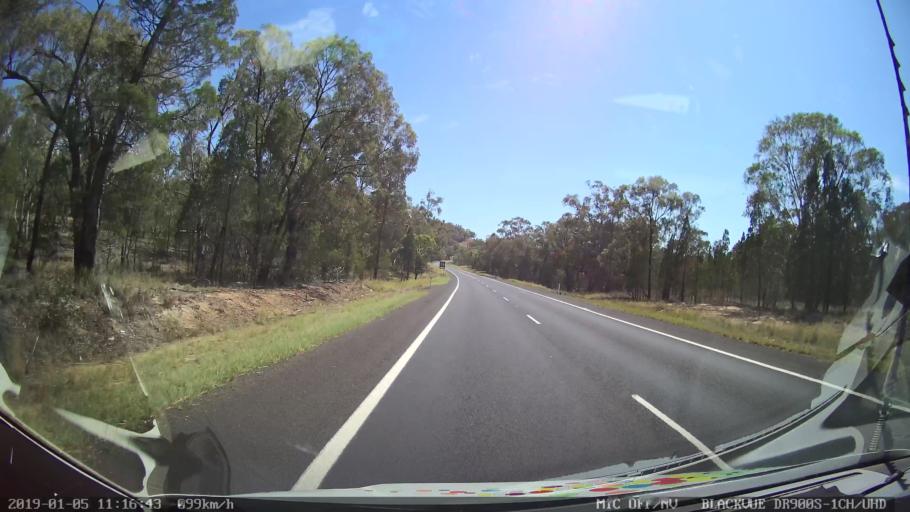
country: AU
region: New South Wales
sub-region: Warrumbungle Shire
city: Coonabarabran
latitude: -31.3352
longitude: 149.3004
